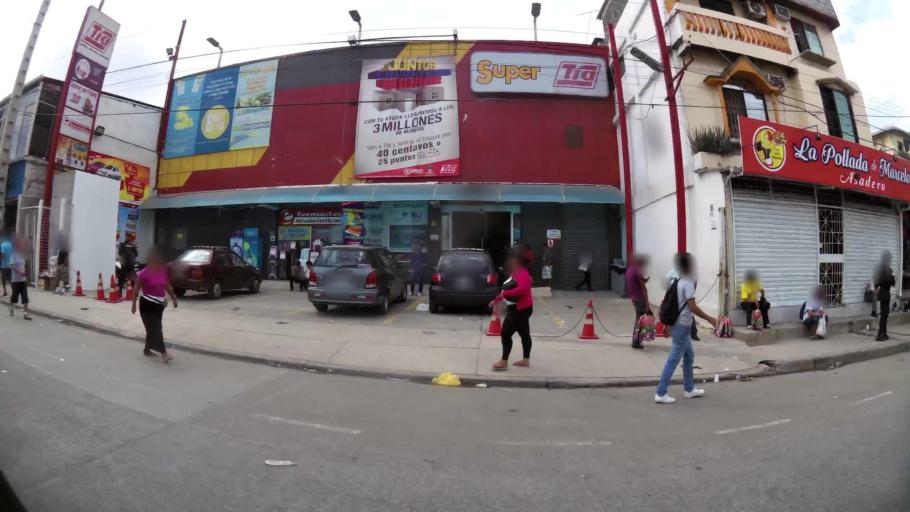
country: EC
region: Guayas
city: Santa Lucia
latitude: -2.1194
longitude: -79.9499
